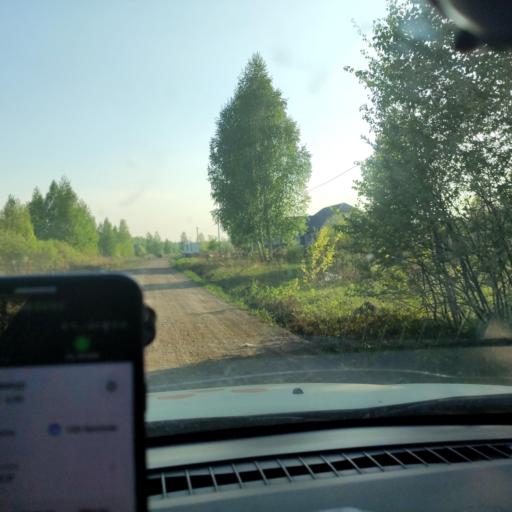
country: RU
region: Bashkortostan
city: Kabakovo
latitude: 54.7263
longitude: 56.2270
